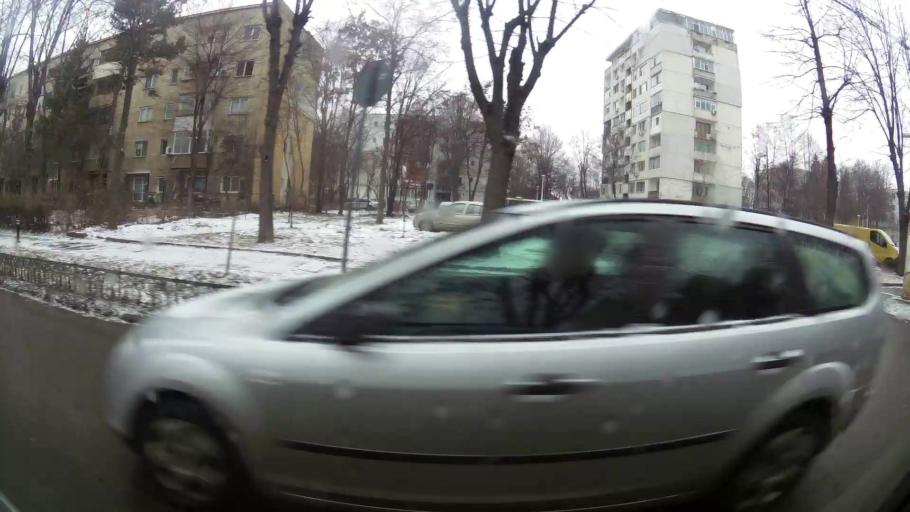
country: RO
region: Prahova
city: Ploiesti
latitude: 44.9576
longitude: 25.9984
